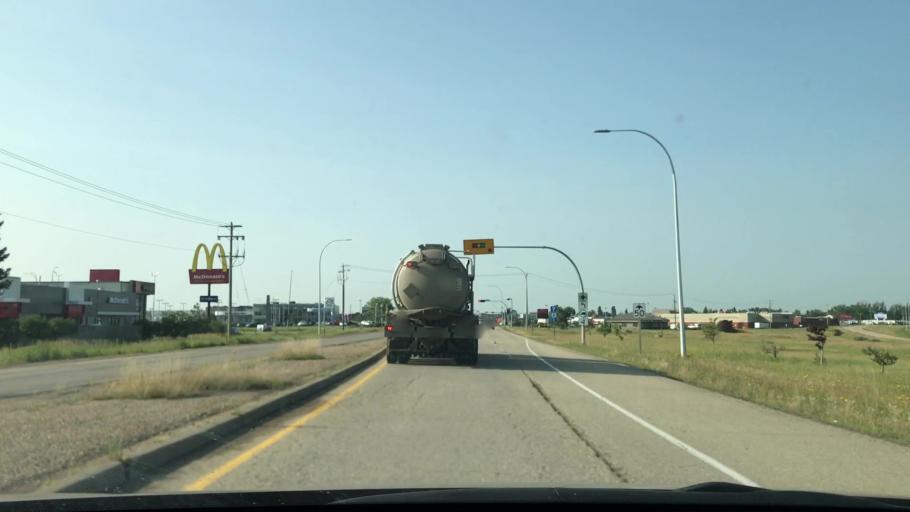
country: CA
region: Alberta
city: Leduc
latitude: 53.2815
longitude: -113.5476
